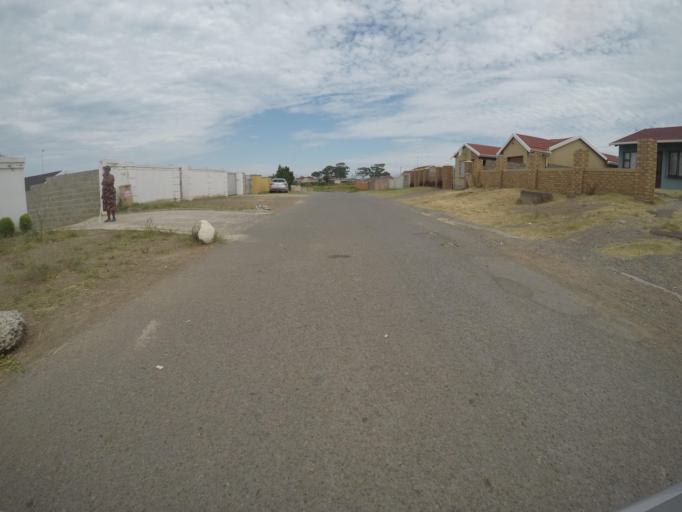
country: ZA
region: Eastern Cape
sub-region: Buffalo City Metropolitan Municipality
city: East London
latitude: -33.0020
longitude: 27.8749
